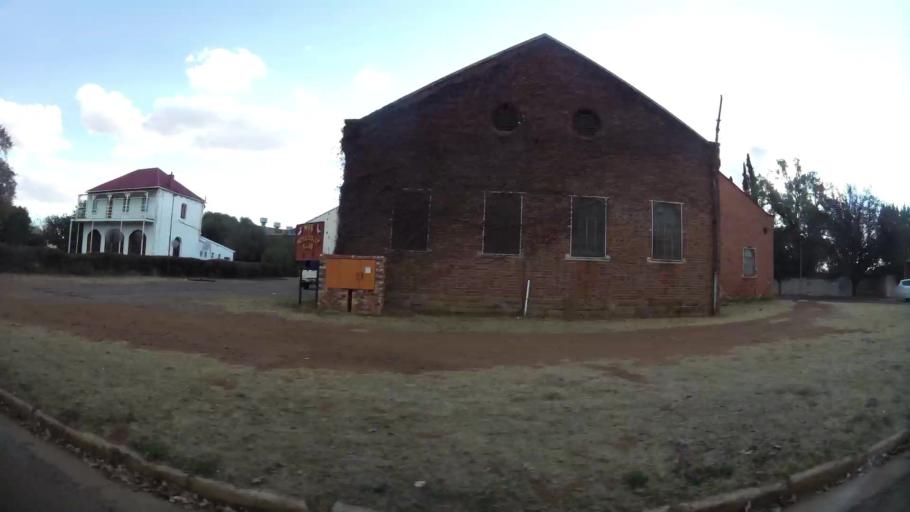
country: ZA
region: North-West
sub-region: Dr Kenneth Kaunda District Municipality
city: Potchefstroom
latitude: -26.7159
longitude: 27.0888
